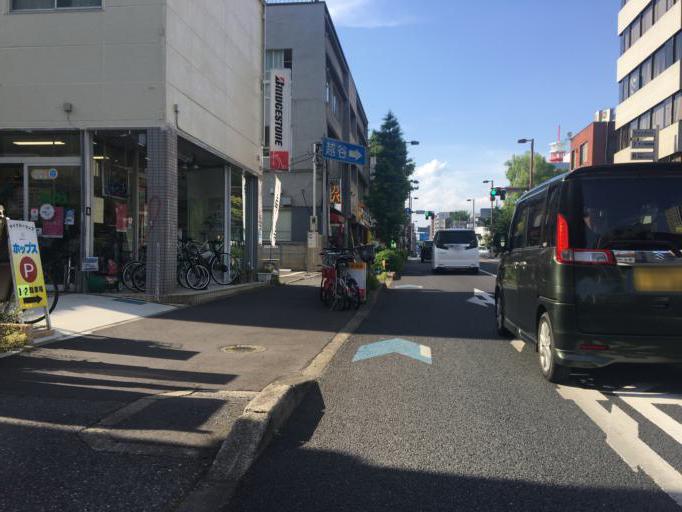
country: JP
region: Saitama
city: Yono
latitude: 35.8602
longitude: 139.6469
